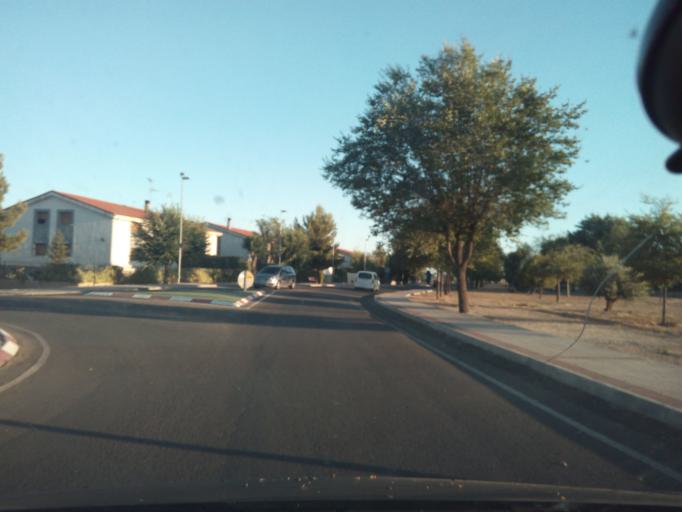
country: ES
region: Castille-La Mancha
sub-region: Province of Toledo
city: Villacanas
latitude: 39.6137
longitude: -3.3366
